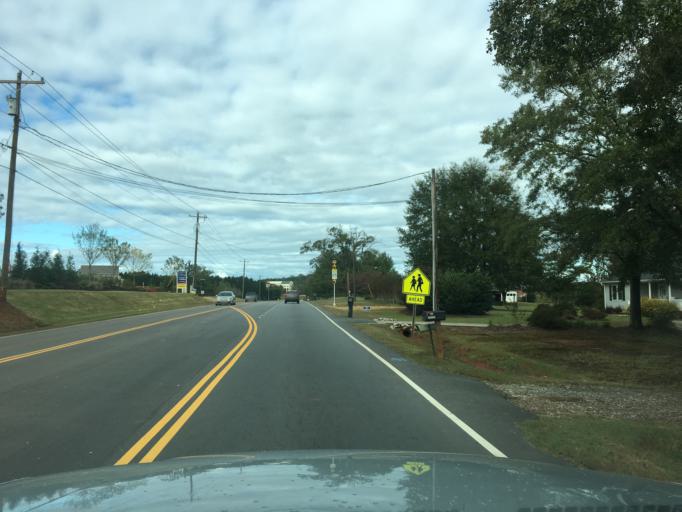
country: US
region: South Carolina
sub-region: Greenville County
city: Greer
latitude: 34.9798
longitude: -82.2249
